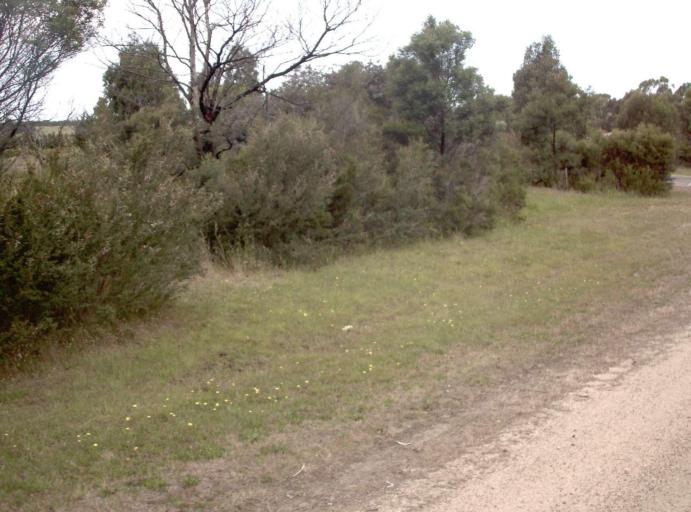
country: AU
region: Victoria
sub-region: Wellington
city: Sale
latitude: -38.1919
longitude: 147.0938
